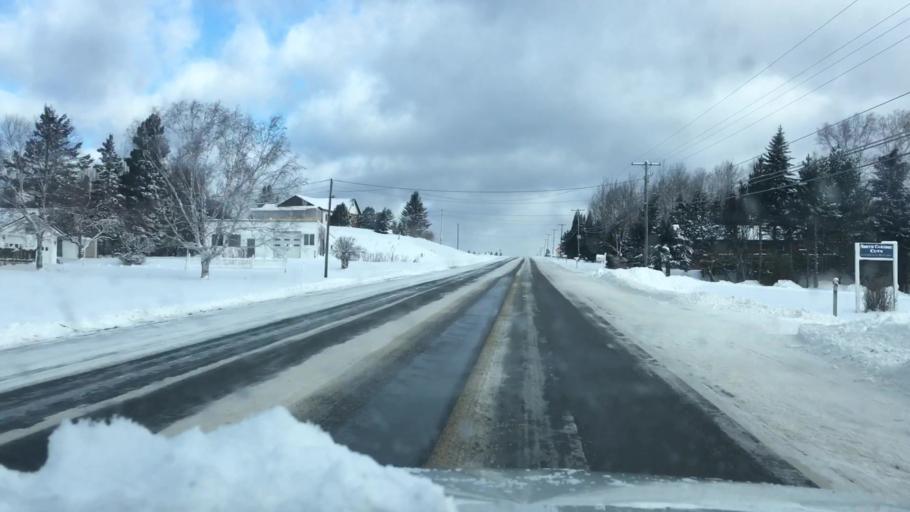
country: US
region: Maine
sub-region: Aroostook County
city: Caribou
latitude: 46.9331
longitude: -68.0234
